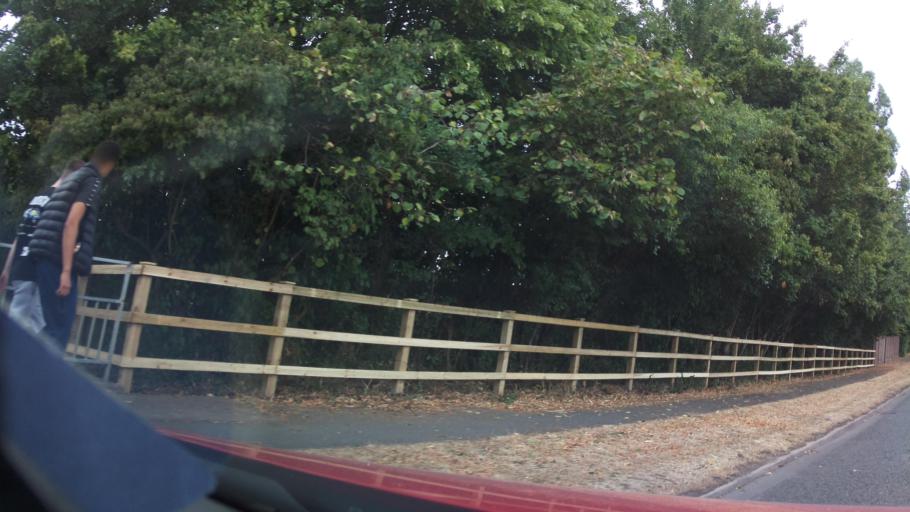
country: GB
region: England
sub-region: Derbyshire
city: Long Eaton
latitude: 52.8970
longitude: -1.2930
